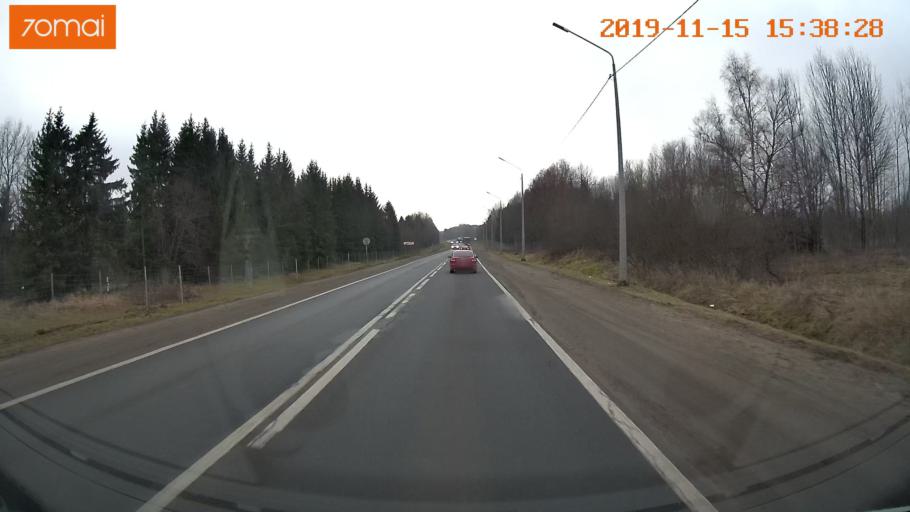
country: RU
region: Jaroslavl
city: Danilov
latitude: 58.0295
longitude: 40.0800
